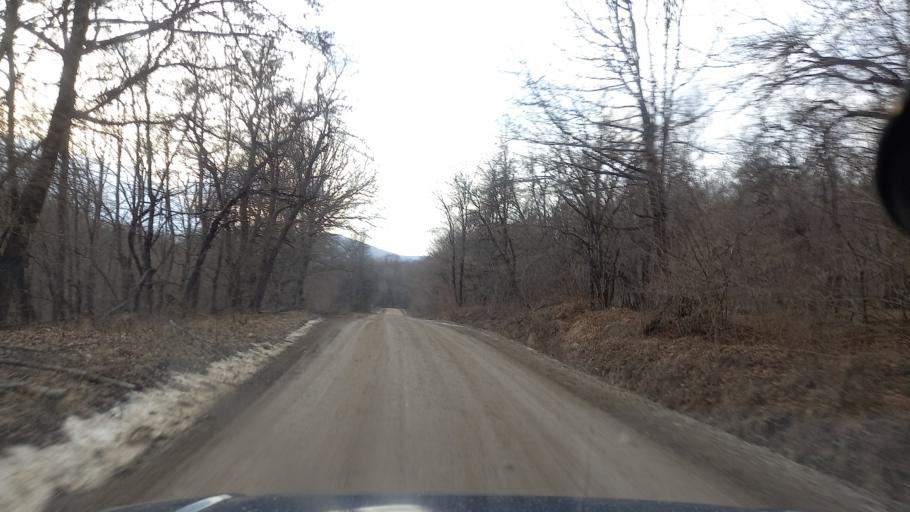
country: RU
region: Adygeya
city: Kamennomostskiy
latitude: 44.1421
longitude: 40.2730
